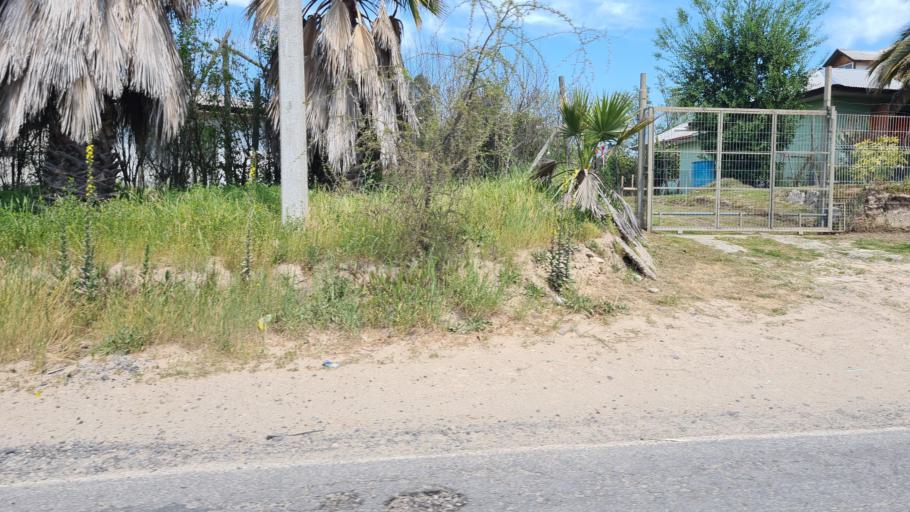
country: CL
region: O'Higgins
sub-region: Provincia de Cachapoal
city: San Vicente
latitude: -34.1582
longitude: -71.4441
